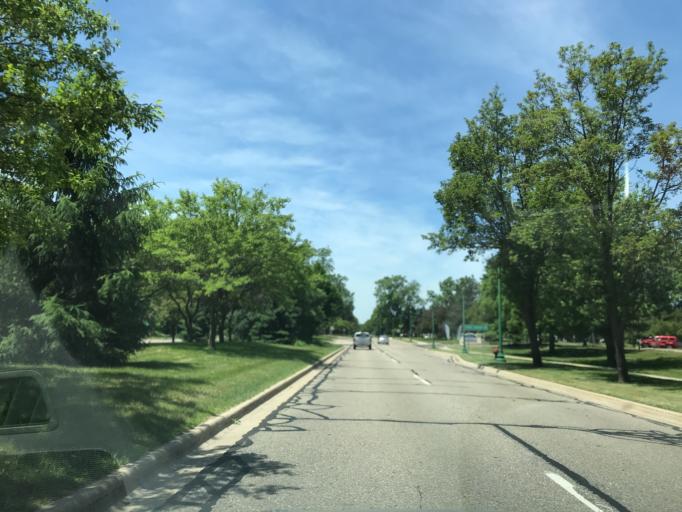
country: US
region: Michigan
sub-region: Oakland County
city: Bingham Farms
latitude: 42.4792
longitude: -83.2676
